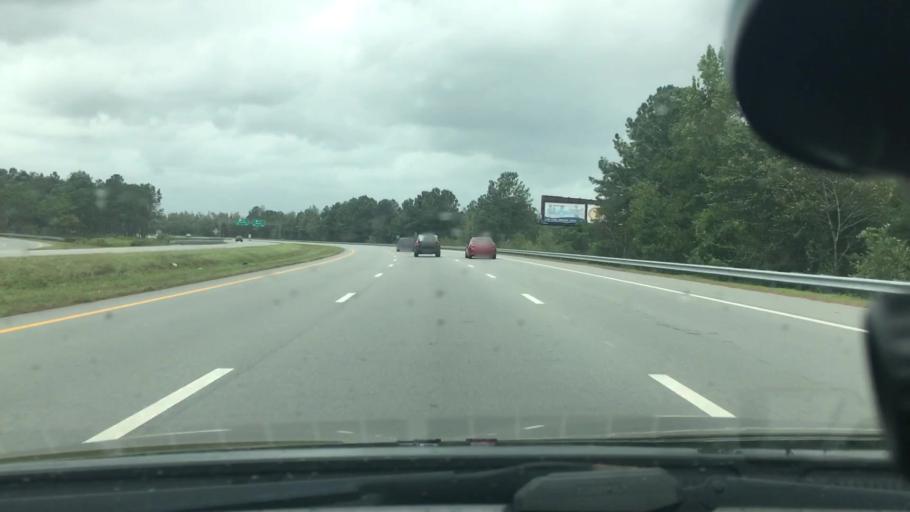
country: US
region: North Carolina
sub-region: Craven County
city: James City
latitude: 35.1081
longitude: -77.0083
